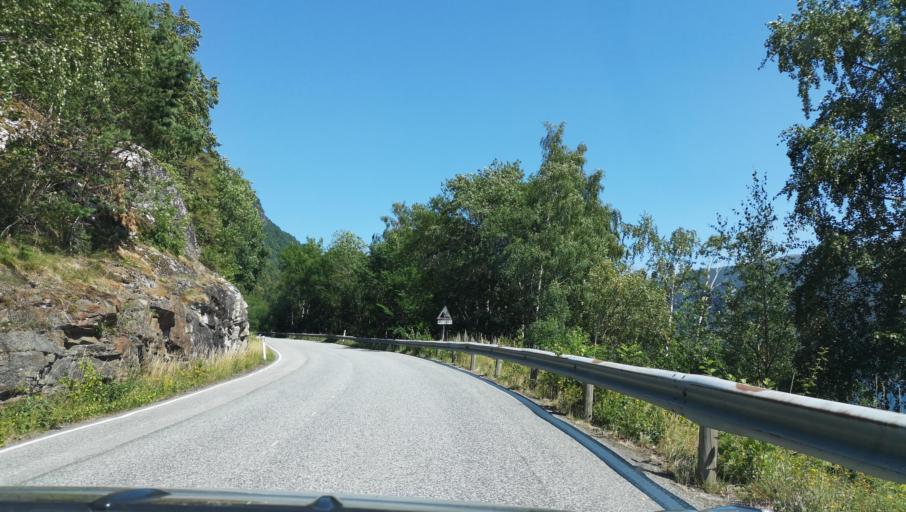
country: NO
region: Hordaland
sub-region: Ulvik
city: Ulvik
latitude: 60.4974
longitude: 6.8959
